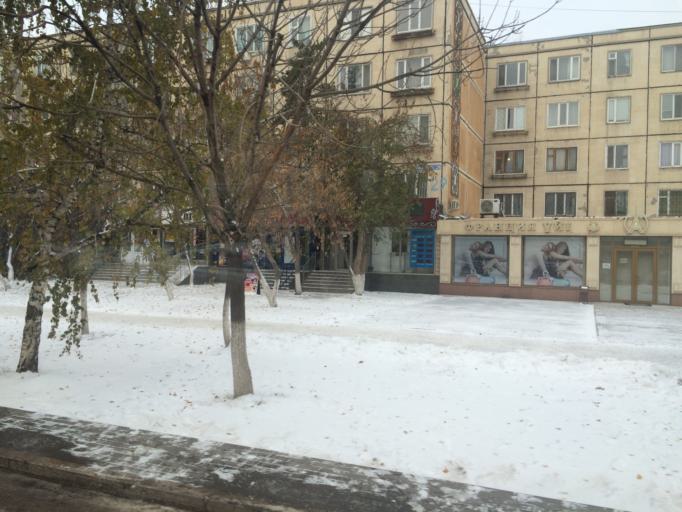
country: KZ
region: Astana Qalasy
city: Astana
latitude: 51.1746
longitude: 71.4189
